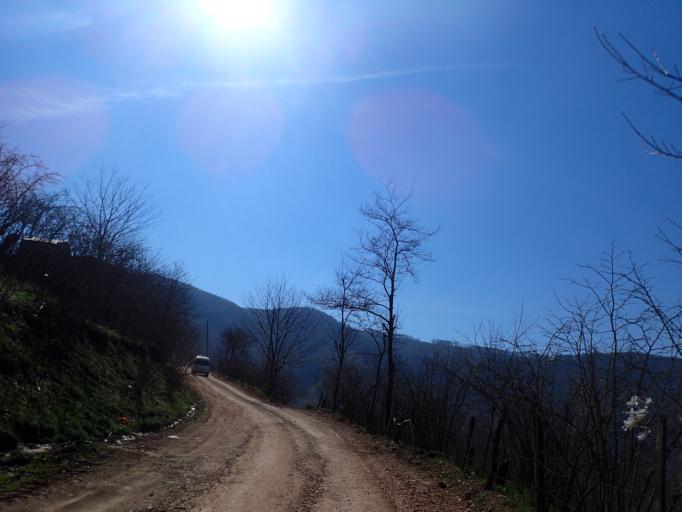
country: TR
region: Ordu
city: Catalpinar
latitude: 40.8677
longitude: 37.4946
